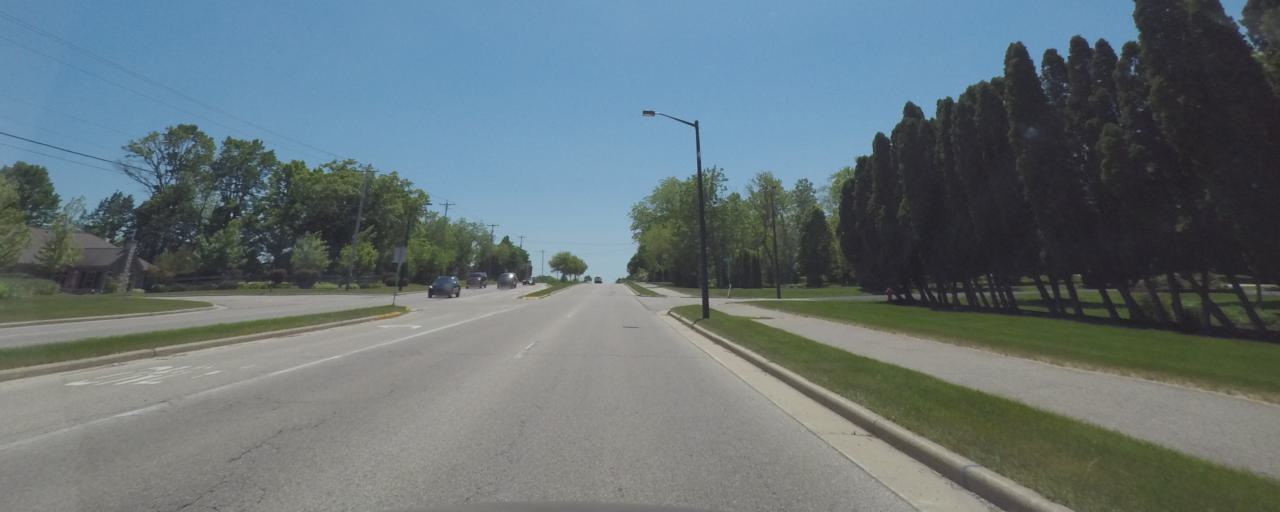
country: US
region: Wisconsin
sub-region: Waukesha County
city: Menomonee Falls
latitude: 43.1420
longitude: -88.1047
